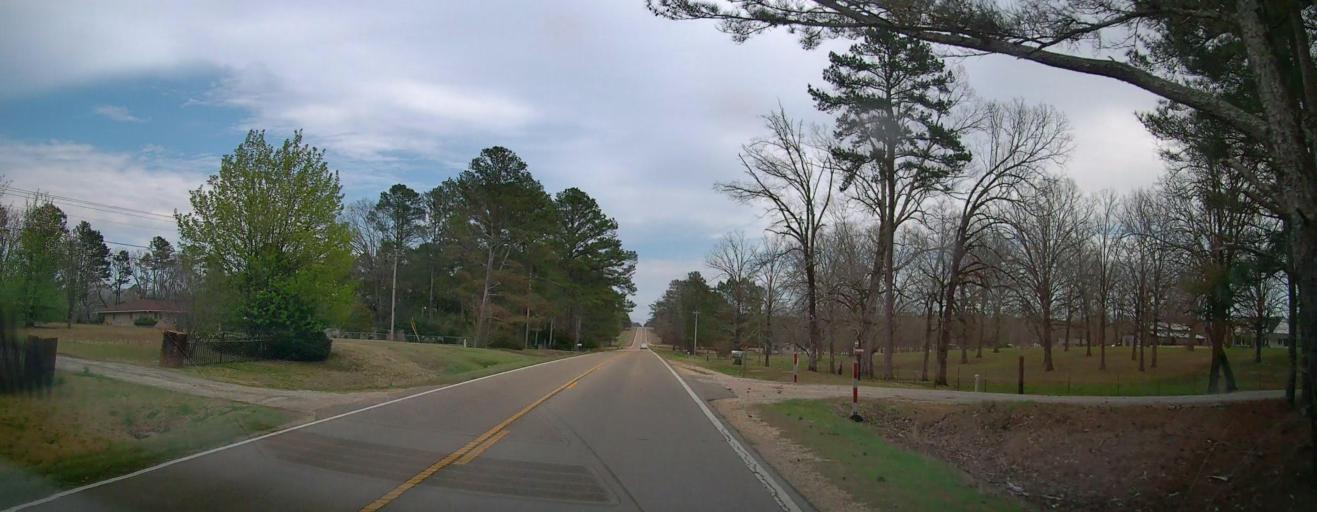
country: US
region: Mississippi
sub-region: Itawamba County
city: Mantachie
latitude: 34.2638
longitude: -88.5392
